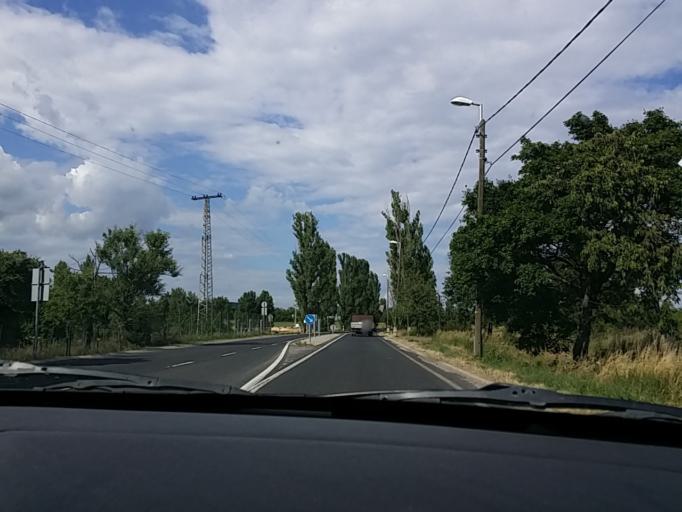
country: HU
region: Veszprem
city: Zanka
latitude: 46.8731
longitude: 17.6840
